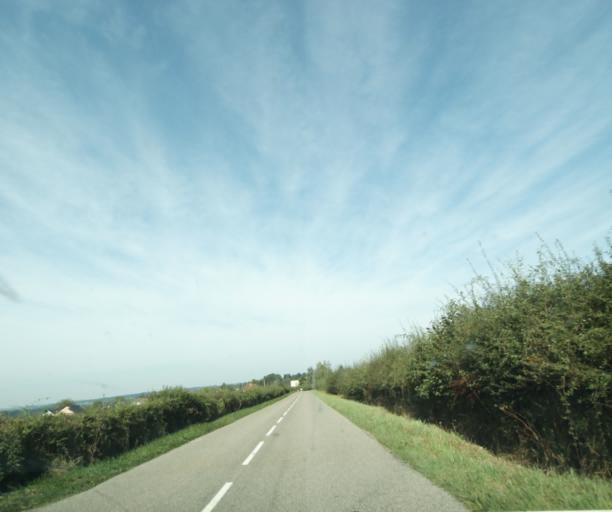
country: FR
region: Bourgogne
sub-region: Departement de Saone-et-Loire
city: Genelard
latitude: 46.5742
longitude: 4.2578
